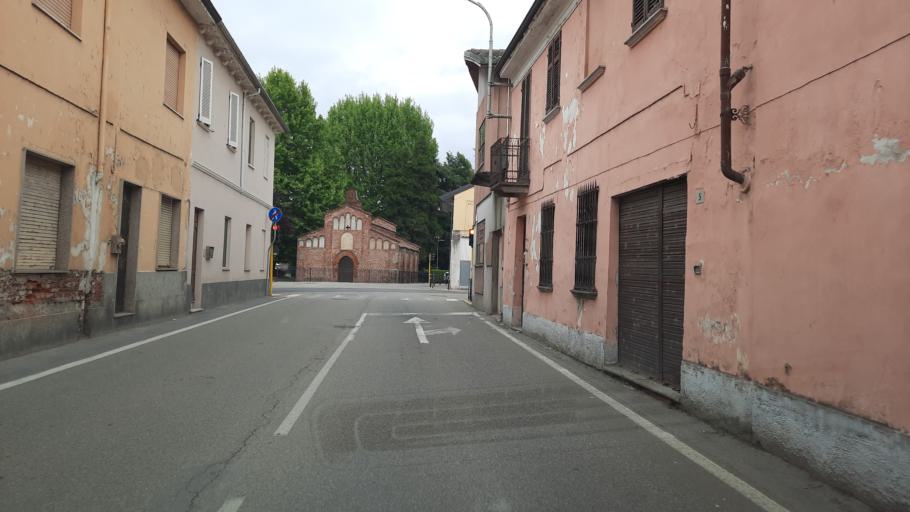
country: IT
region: Lombardy
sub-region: Provincia di Pavia
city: Robbio
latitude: 45.2877
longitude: 8.5942
